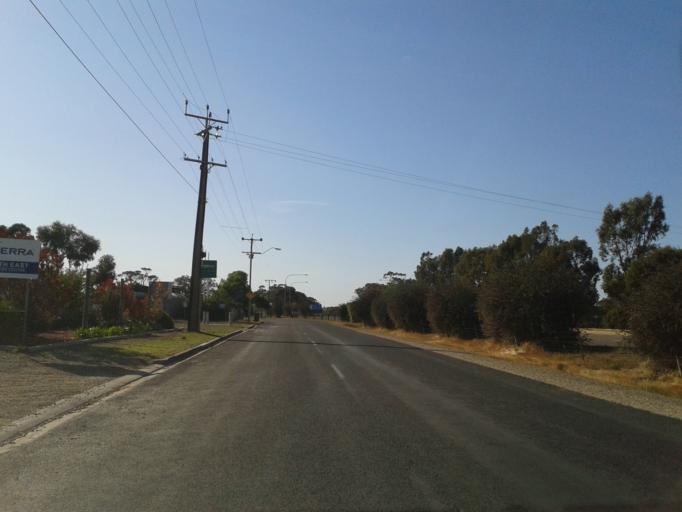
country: AU
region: South Australia
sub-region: Tatiara
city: Bordertown
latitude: -36.3019
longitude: 140.7635
